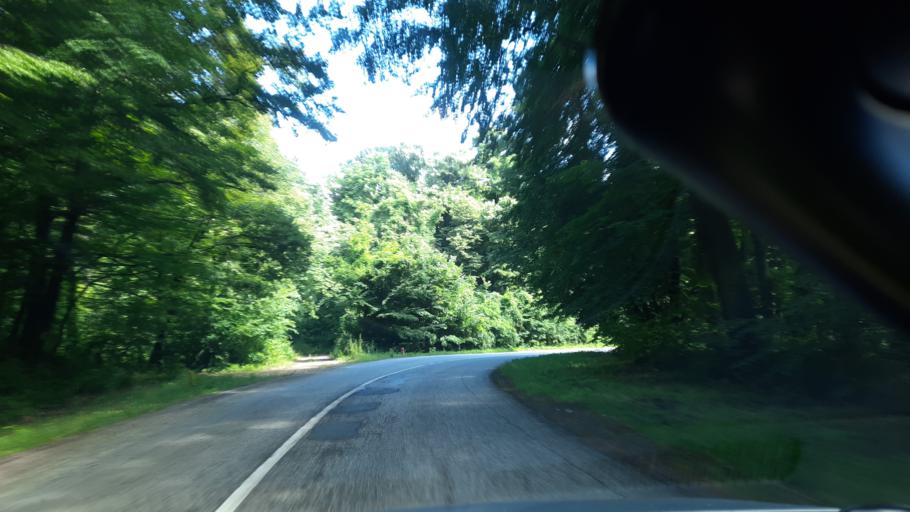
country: RS
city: Glozan
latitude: 45.1441
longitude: 19.5802
